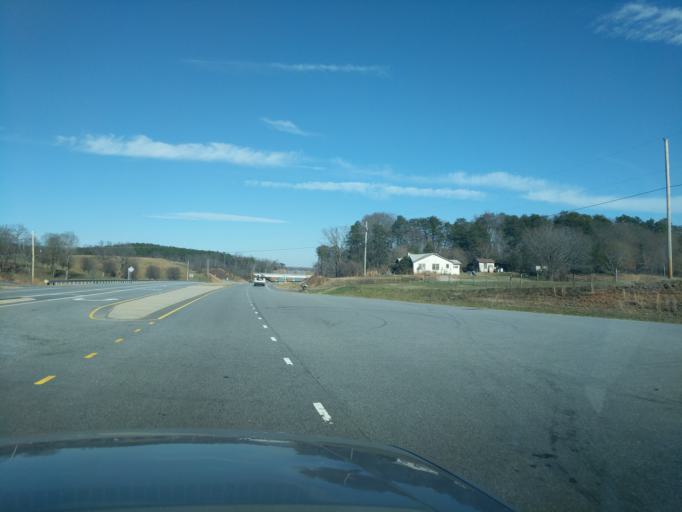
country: US
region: South Carolina
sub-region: Spartanburg County
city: Mayo
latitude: 35.1857
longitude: -81.8437
